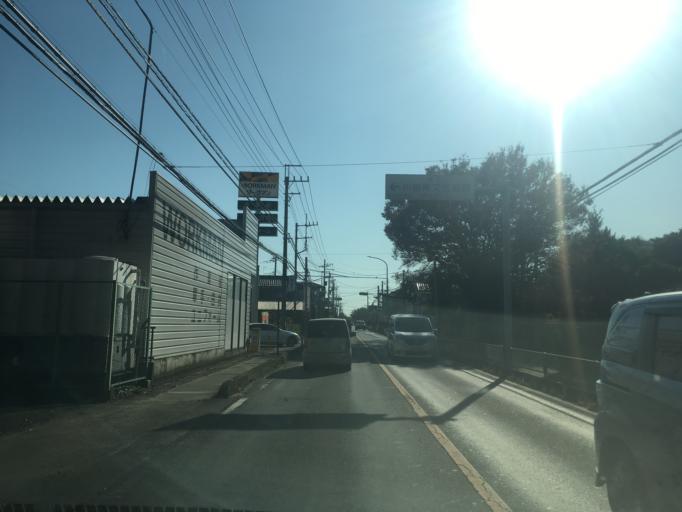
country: JP
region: Saitama
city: Kawagoe
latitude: 35.8727
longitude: 139.4734
